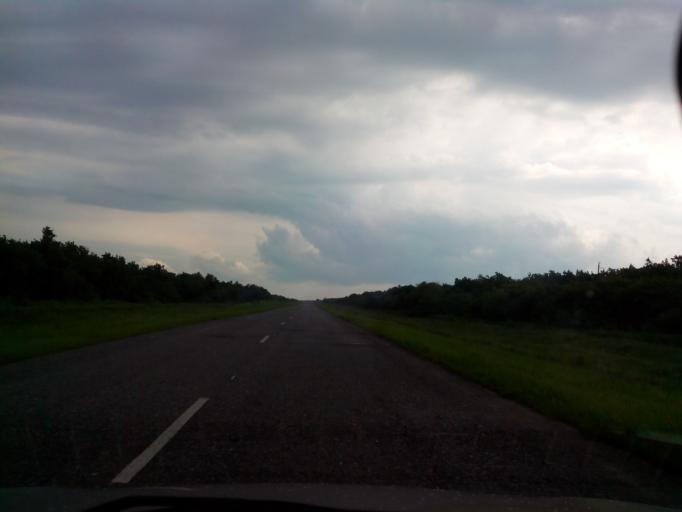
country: RU
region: Volgograd
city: Kumylzhenskaya
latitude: 49.8925
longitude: 42.8120
